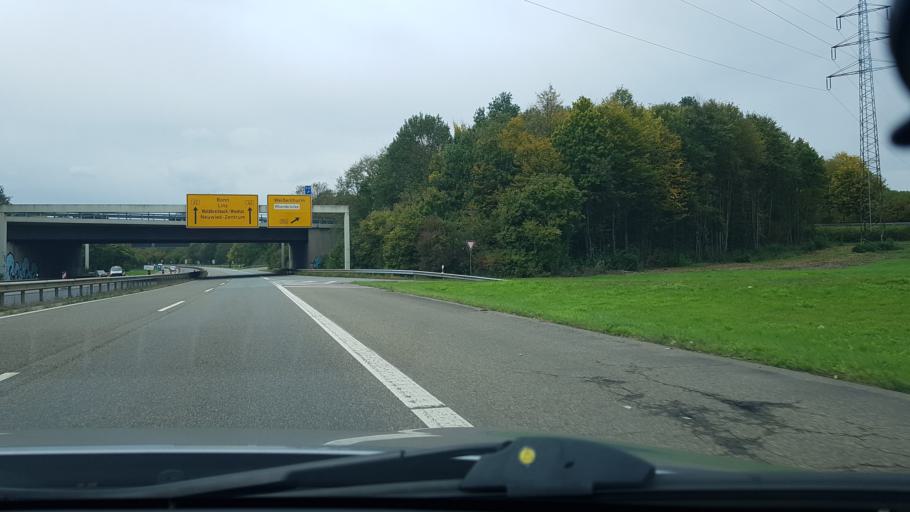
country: DE
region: Rheinland-Pfalz
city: Neuwied
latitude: 50.4415
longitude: 7.4866
